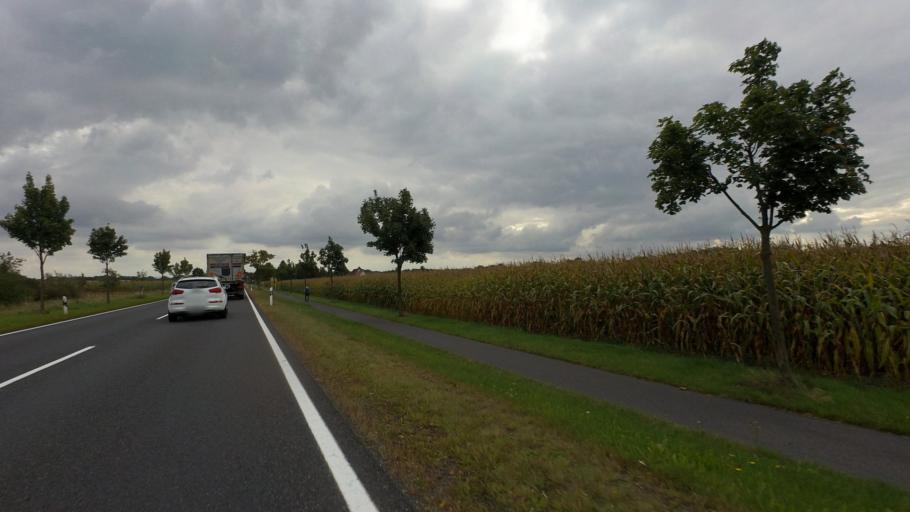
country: DE
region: Saxony
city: Neschwitz
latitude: 51.2784
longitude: 14.3376
